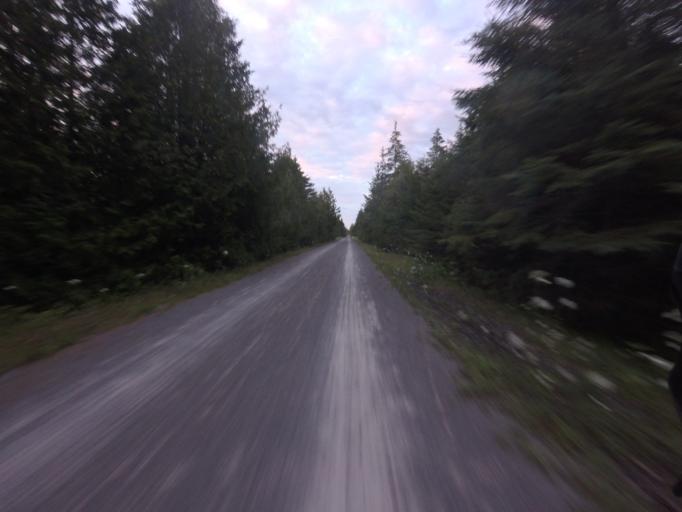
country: CA
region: Ontario
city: Bells Corners
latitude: 45.2300
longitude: -75.9655
